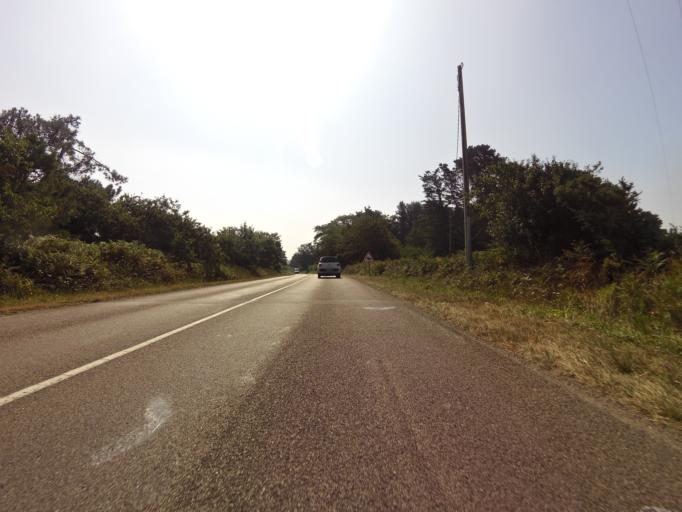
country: FR
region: Brittany
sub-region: Departement du Finistere
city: Plozevet
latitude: 48.0005
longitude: -4.4443
